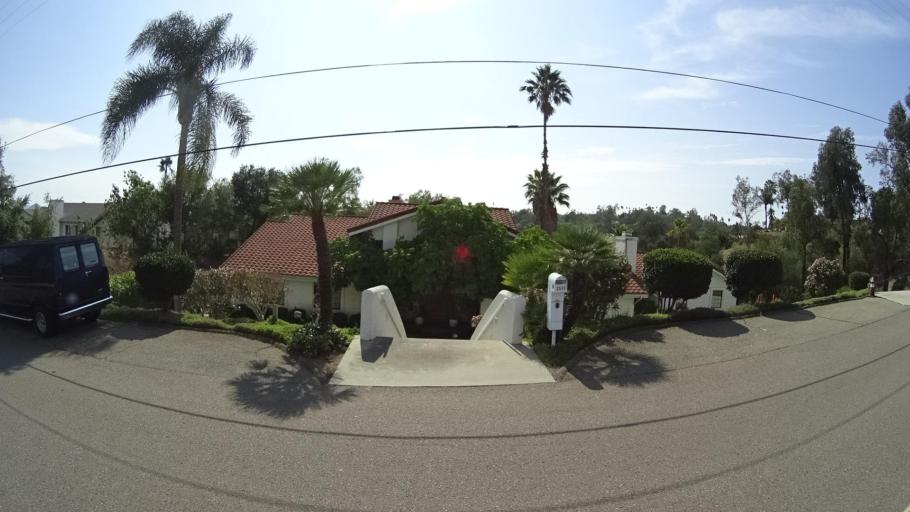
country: US
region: California
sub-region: San Diego County
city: Escondido
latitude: 33.0893
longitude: -117.0615
